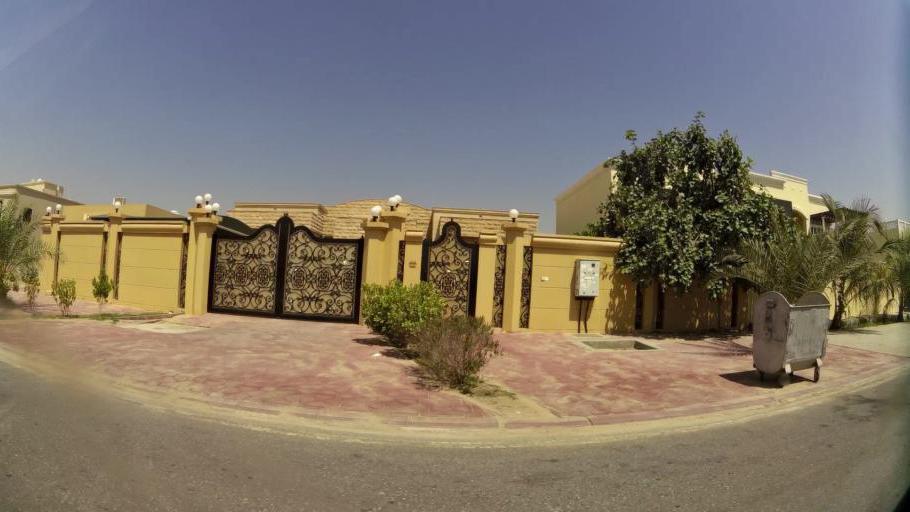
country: AE
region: Ajman
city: Ajman
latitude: 25.4218
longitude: 55.5236
